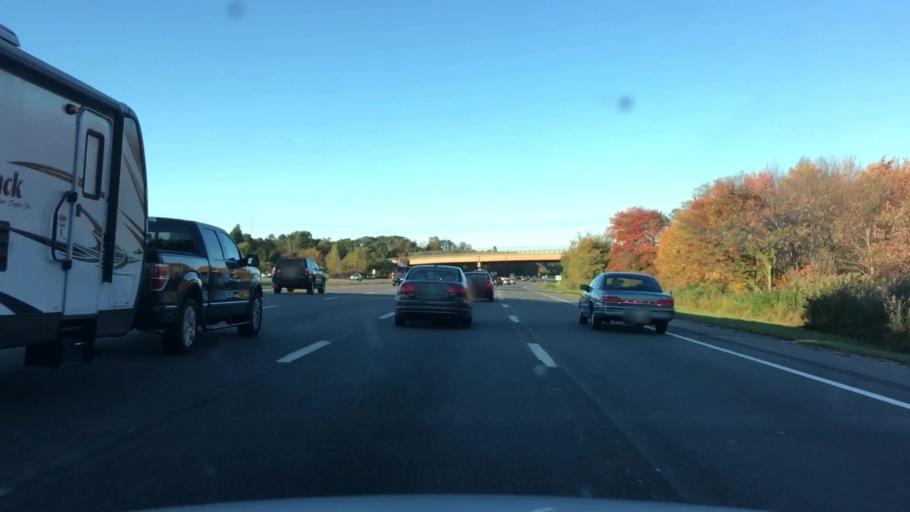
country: US
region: New Hampshire
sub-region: Rockingham County
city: North Hampton
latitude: 42.9912
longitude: -70.8497
